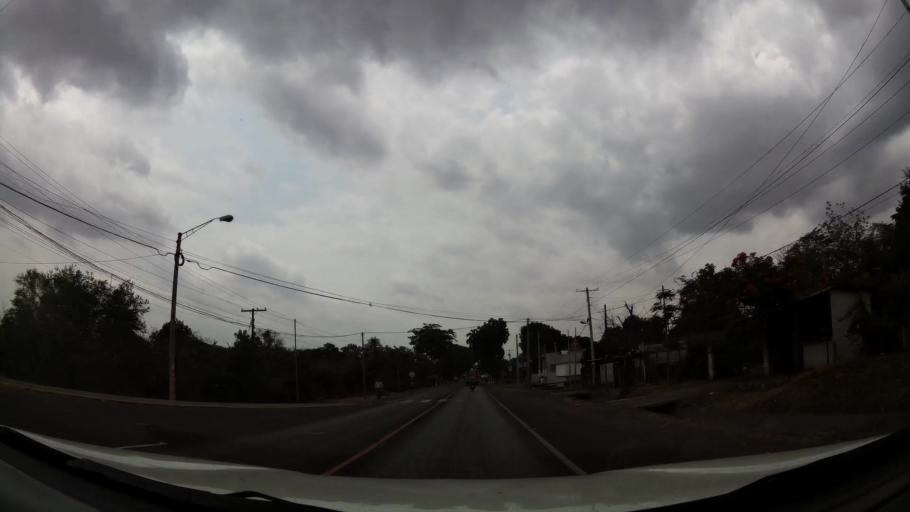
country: NI
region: Leon
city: Leon
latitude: 12.4610
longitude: -86.8674
